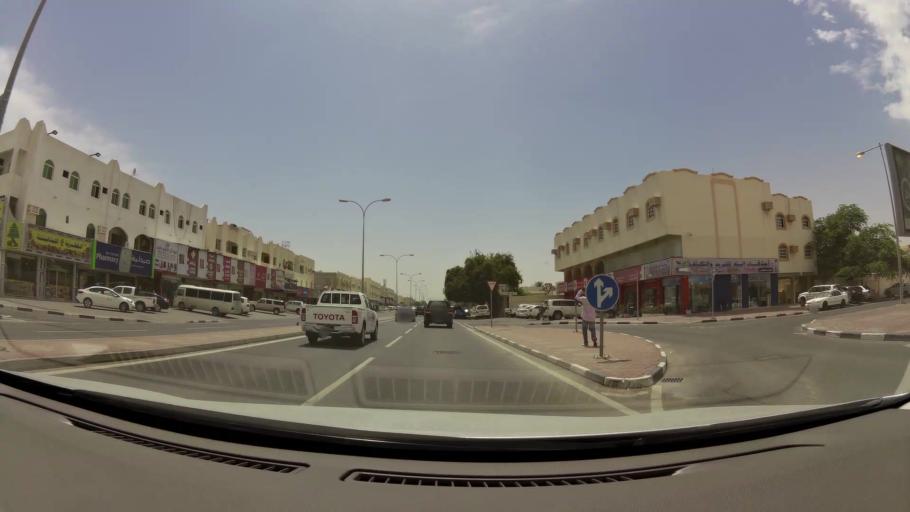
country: QA
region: Baladiyat ar Rayyan
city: Ar Rayyan
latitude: 25.2929
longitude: 51.4199
